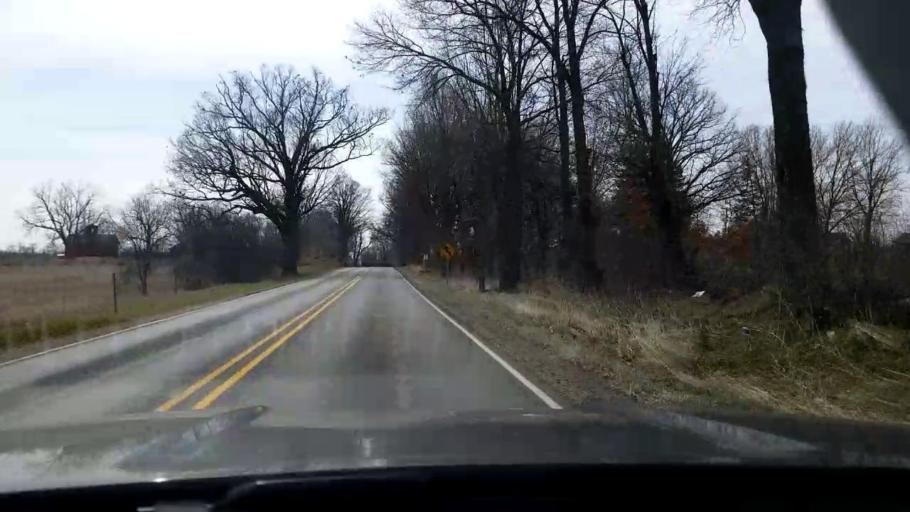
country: US
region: Michigan
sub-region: Jackson County
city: Spring Arbor
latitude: 42.1632
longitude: -84.5198
